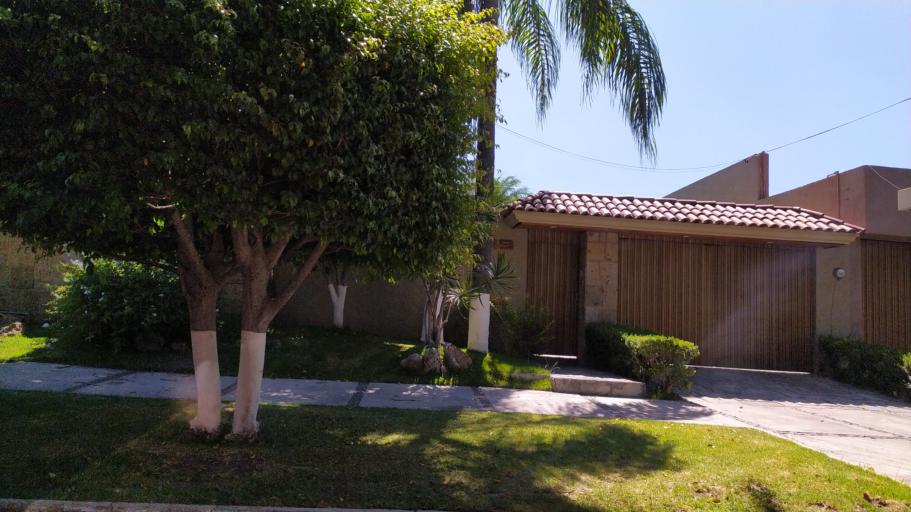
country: MX
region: Jalisco
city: Guadalajara
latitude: 20.6794
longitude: -103.4055
